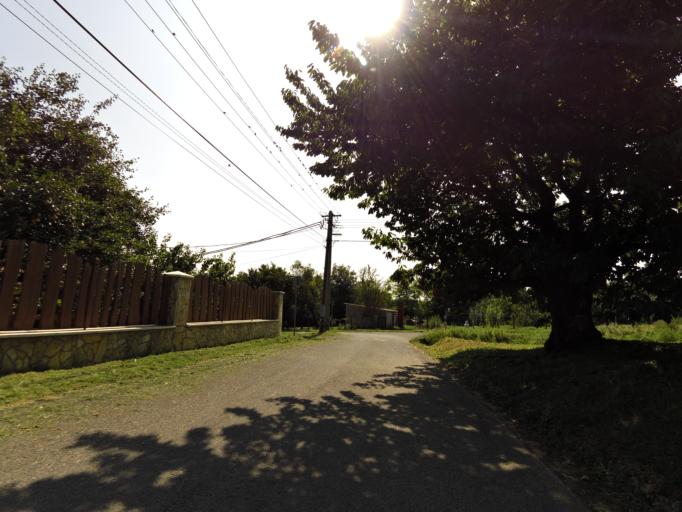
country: HU
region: Zala
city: Vonyarcvashegy
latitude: 46.8140
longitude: 17.3783
